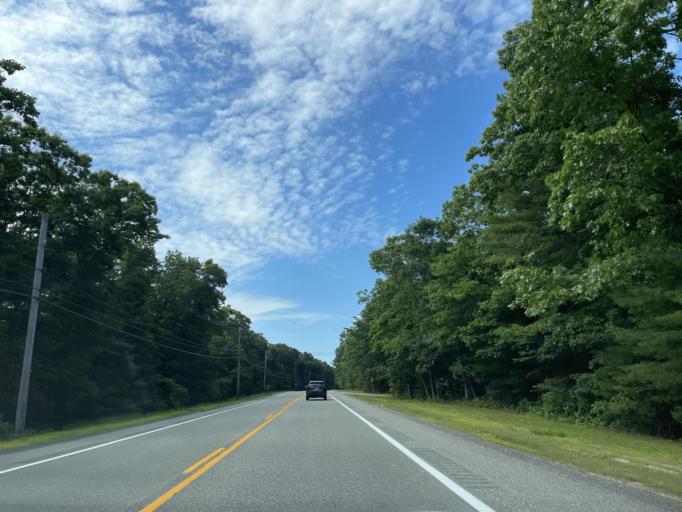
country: US
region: Rhode Island
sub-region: Kent County
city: West Greenwich
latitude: 41.6543
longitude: -71.6943
